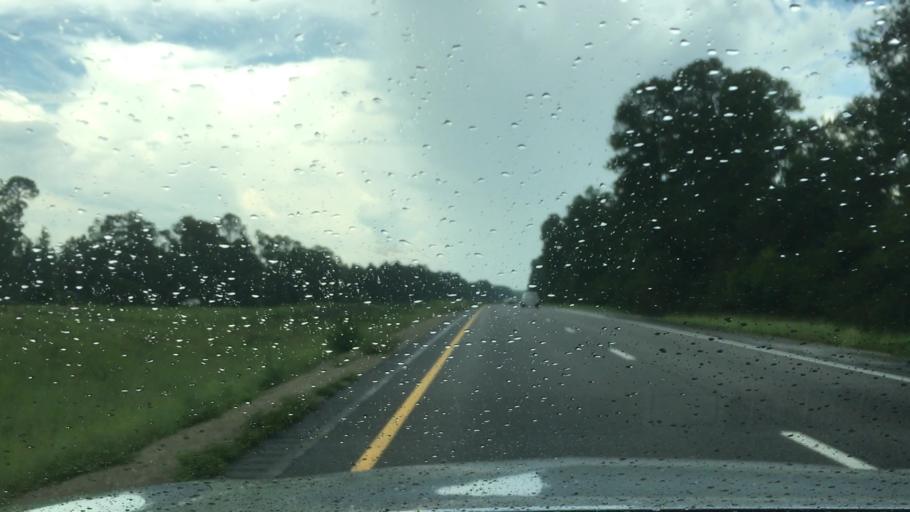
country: US
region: Mississippi
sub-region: Lamar County
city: Purvis
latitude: 31.2036
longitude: -89.3359
